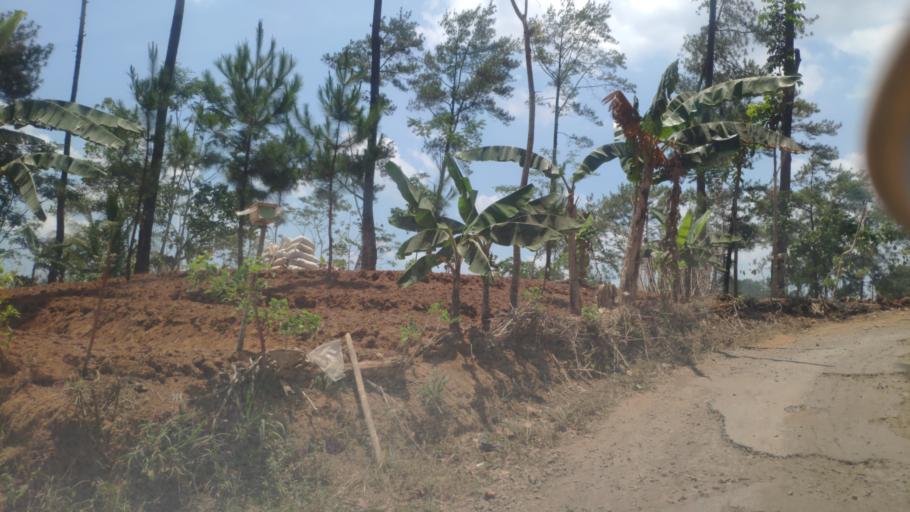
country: ID
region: Central Java
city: Gombong
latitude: -7.4818
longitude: 109.6437
